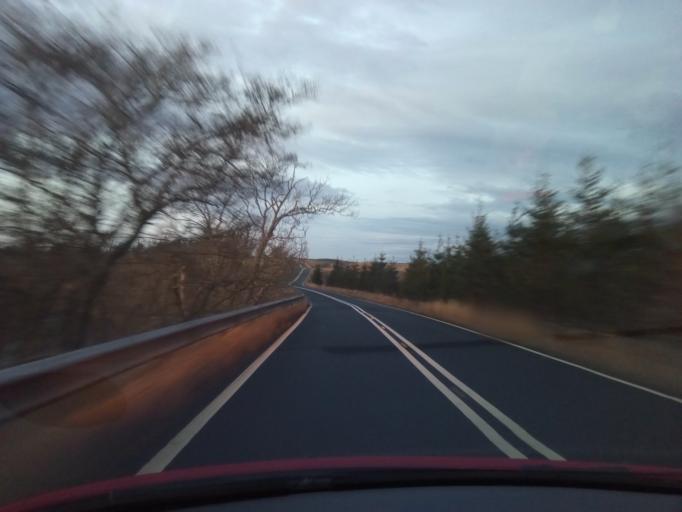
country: GB
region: England
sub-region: Northumberland
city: Rochester
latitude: 55.2466
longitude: -2.2176
